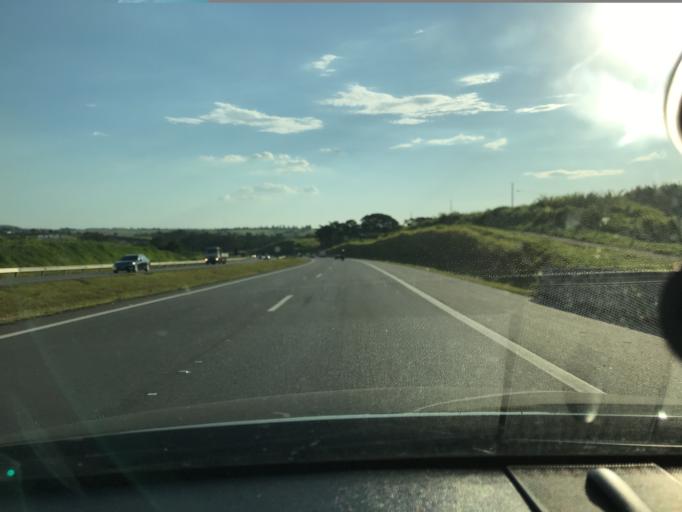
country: BR
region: Sao Paulo
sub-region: Valinhos
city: Valinhos
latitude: -23.0019
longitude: -47.0808
